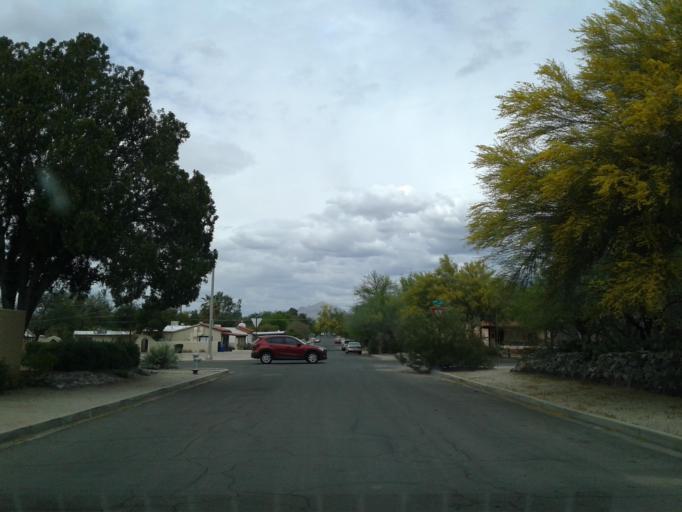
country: US
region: Arizona
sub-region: Pima County
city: Tucson
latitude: 32.2262
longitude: -110.9366
